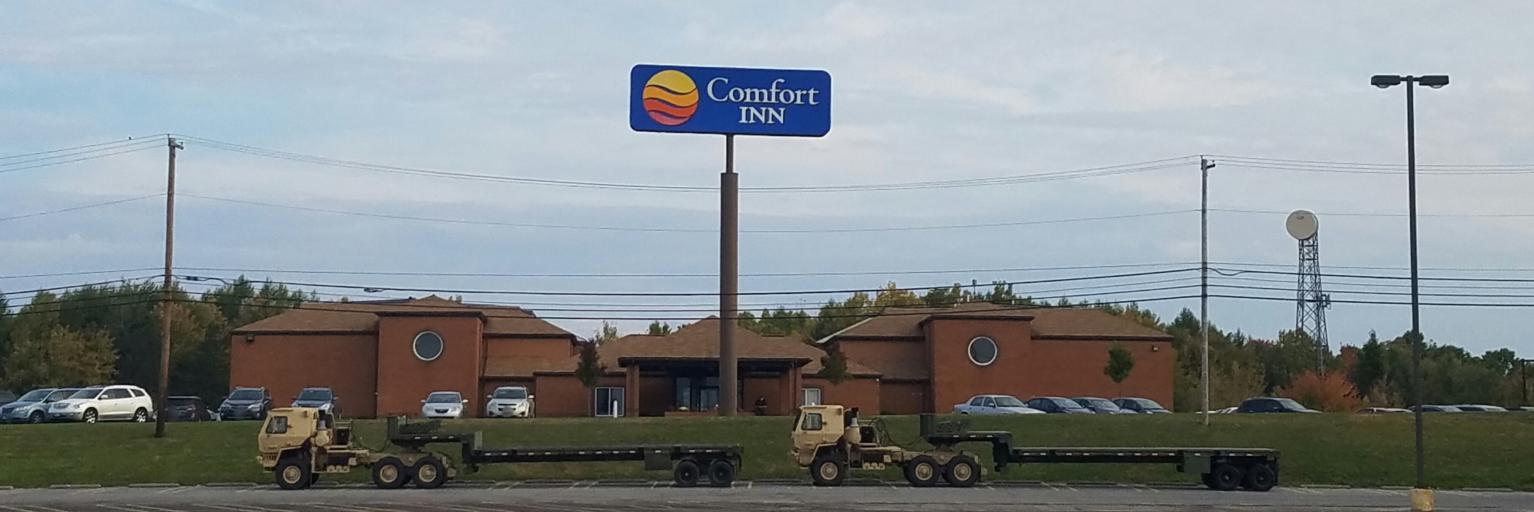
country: US
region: Pennsylvania
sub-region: Clarion County
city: Clarion
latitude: 41.1941
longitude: -79.3940
